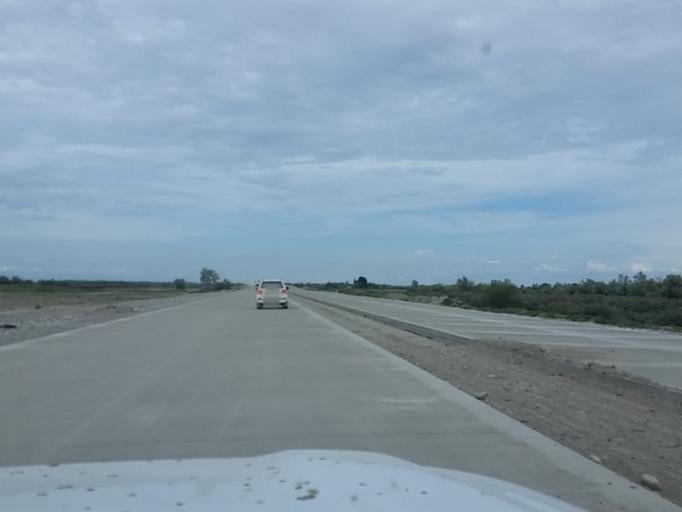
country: KZ
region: Almaty Oblysy
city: Zharkent
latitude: 44.0237
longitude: 79.8369
